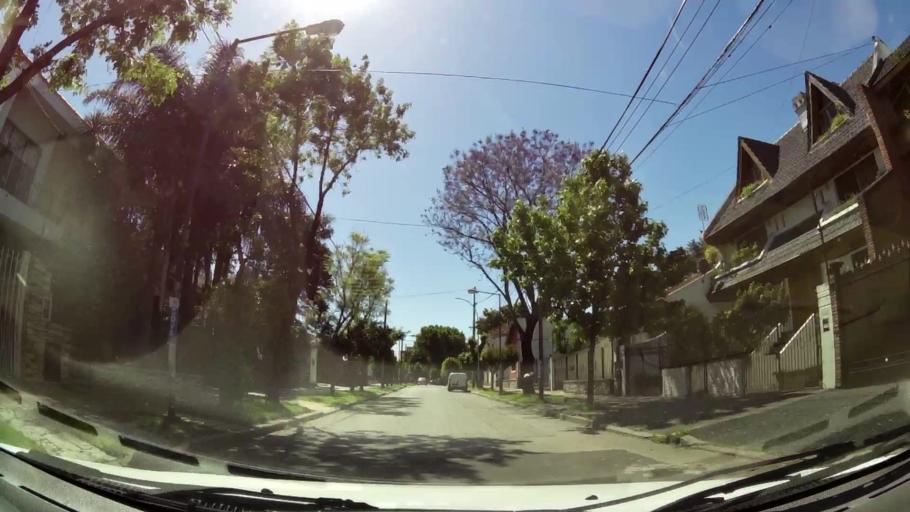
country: AR
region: Buenos Aires
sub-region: Partido de General San Martin
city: General San Martin
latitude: -34.5575
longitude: -58.5542
